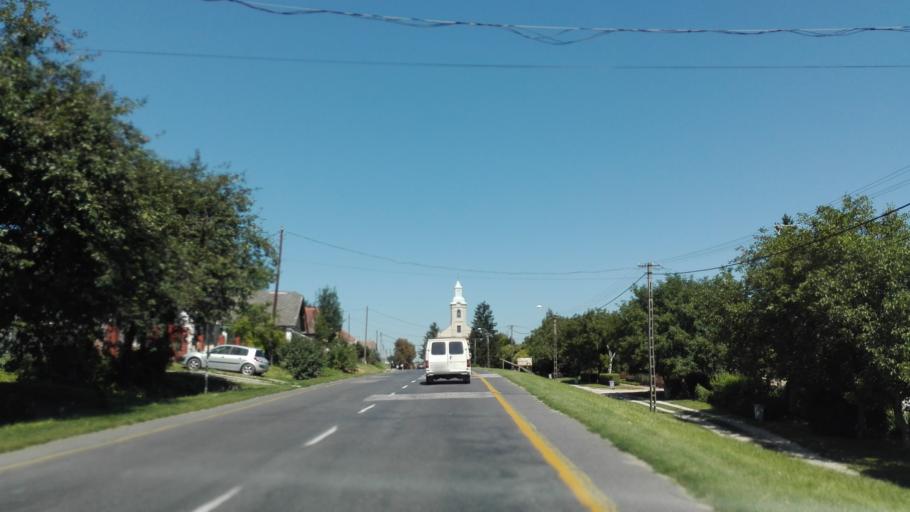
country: HU
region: Tolna
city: Simontornya
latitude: 46.7726
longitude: 18.5160
